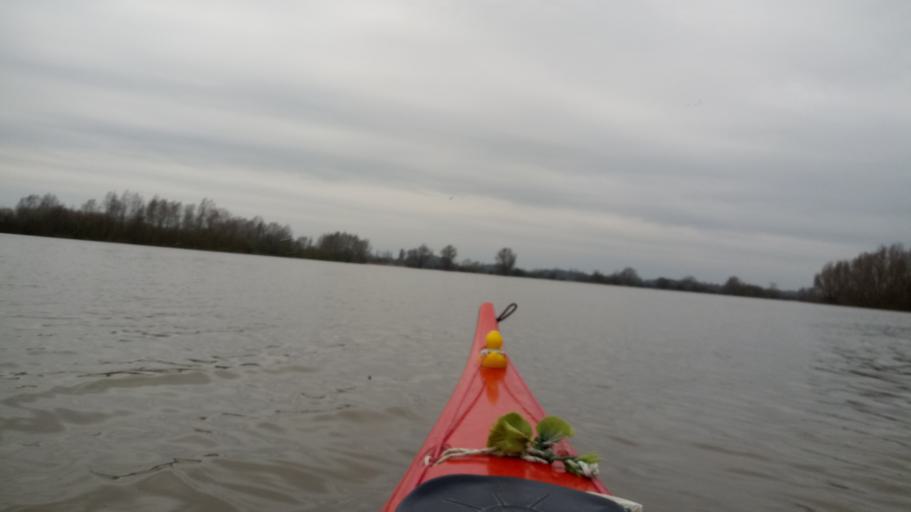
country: NL
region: Gelderland
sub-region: Gemeente Lochem
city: Gorssel
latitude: 52.1792
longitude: 6.1814
